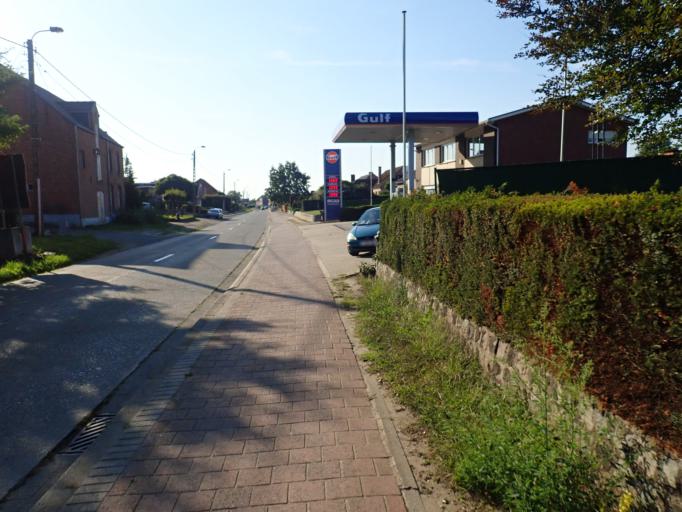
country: BE
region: Flanders
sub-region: Provincie Antwerpen
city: Heist-op-den-Berg
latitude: 51.0999
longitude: 4.7470
